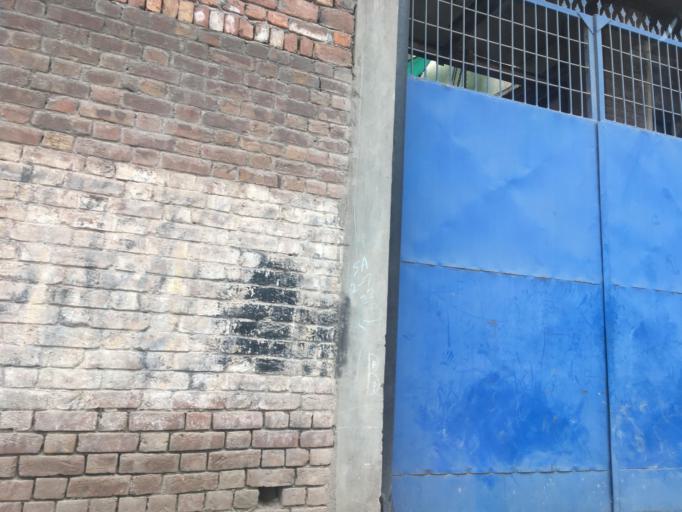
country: PK
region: Punjab
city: Lahore
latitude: 31.6124
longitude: 74.3506
